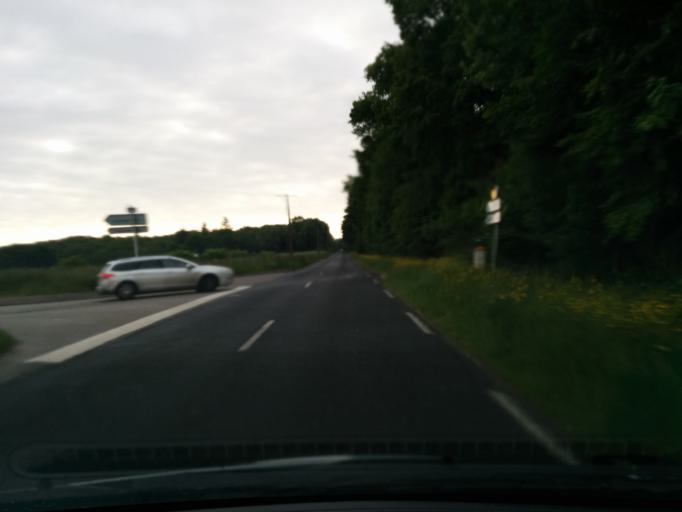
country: FR
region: Haute-Normandie
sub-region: Departement de l'Eure
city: Gasny
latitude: 49.0948
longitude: 1.5707
